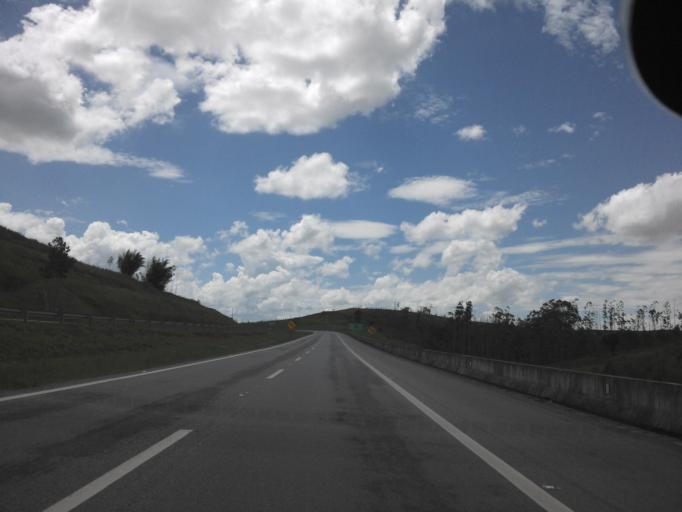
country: BR
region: Sao Paulo
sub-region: Jacarei
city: Jacarei
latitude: -23.3334
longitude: -46.0243
